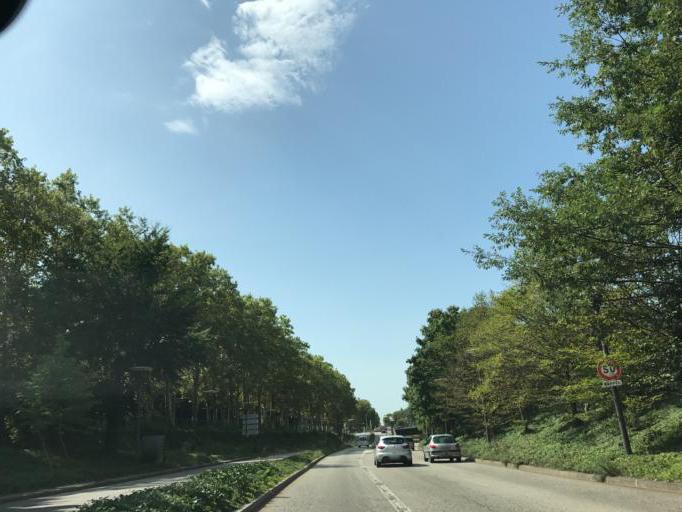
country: FR
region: Rhone-Alpes
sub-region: Departement du Rhone
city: Caluire-et-Cuire
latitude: 45.7804
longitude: 4.8460
